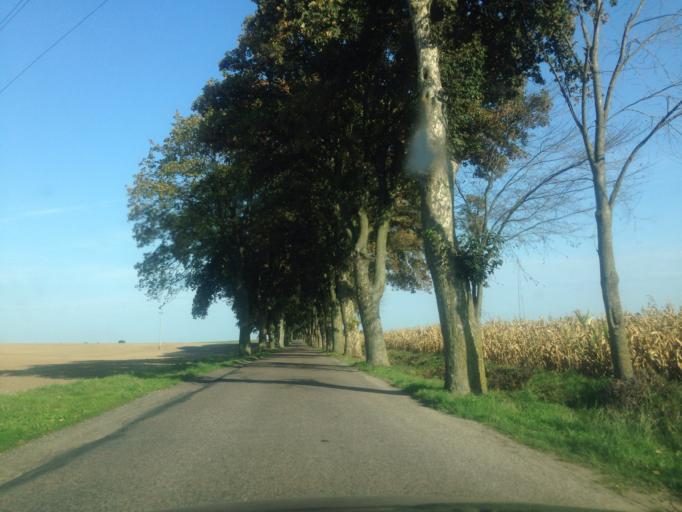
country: PL
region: Kujawsko-Pomorskie
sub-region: Powiat brodnicki
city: Brzozie
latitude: 53.3284
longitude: 19.5512
